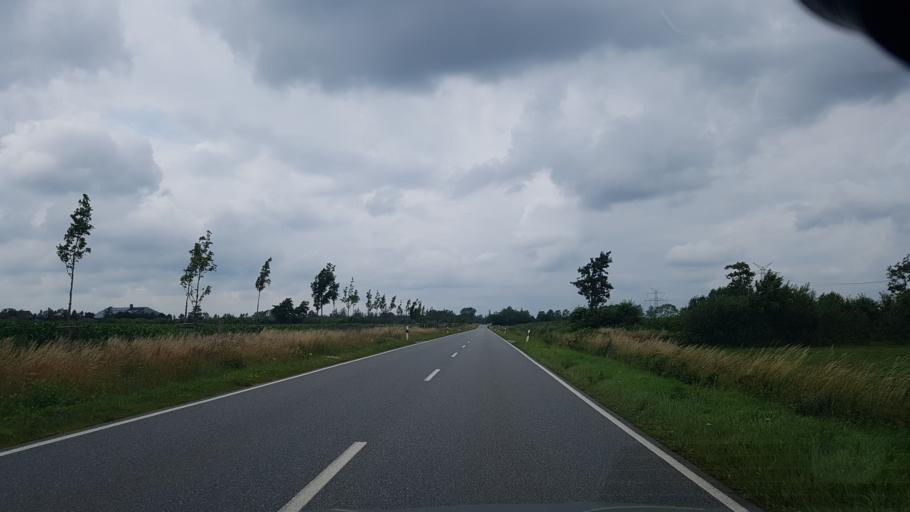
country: DE
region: Schleswig-Holstein
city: Osterby
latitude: 54.8109
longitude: 9.2334
